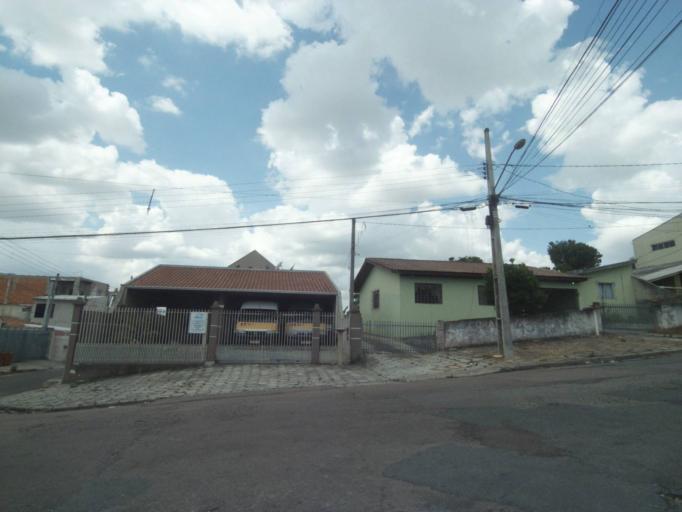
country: BR
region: Parana
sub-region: Sao Jose Dos Pinhais
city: Sao Jose dos Pinhais
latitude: -25.5345
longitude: -49.2762
